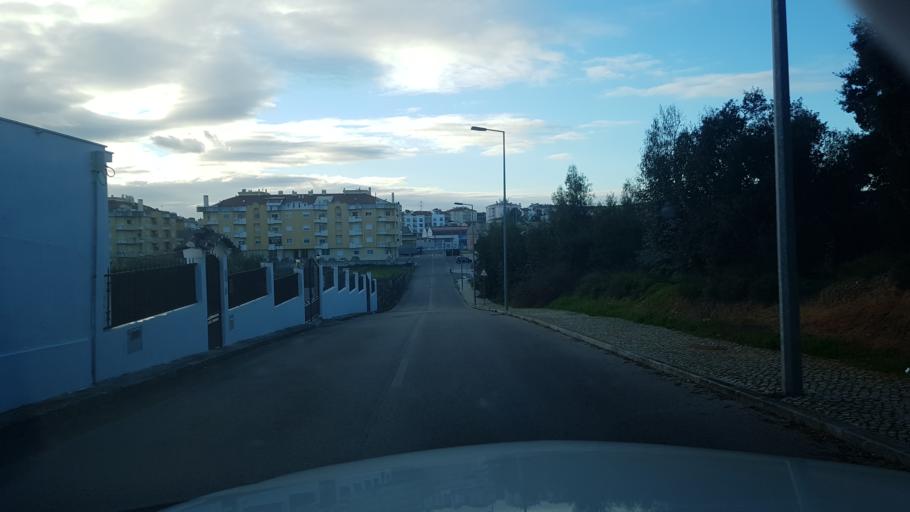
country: PT
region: Santarem
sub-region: Entroncamento
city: Entroncamento
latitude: 39.4748
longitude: -8.4705
